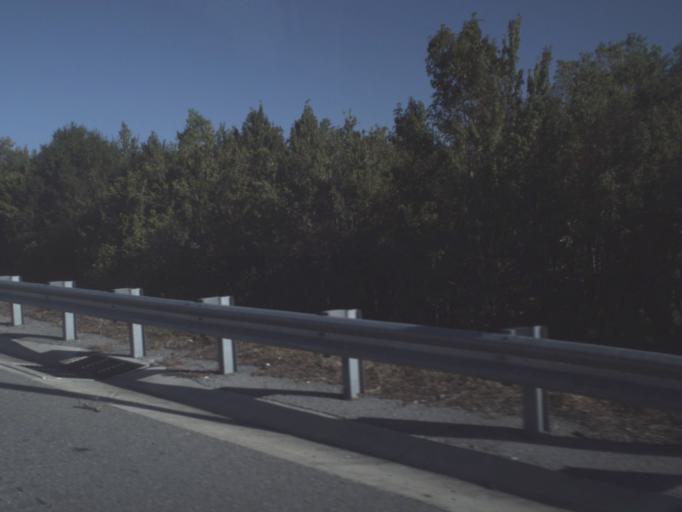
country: US
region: Florida
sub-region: Seminole County
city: Midway
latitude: 28.7470
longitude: -81.2635
